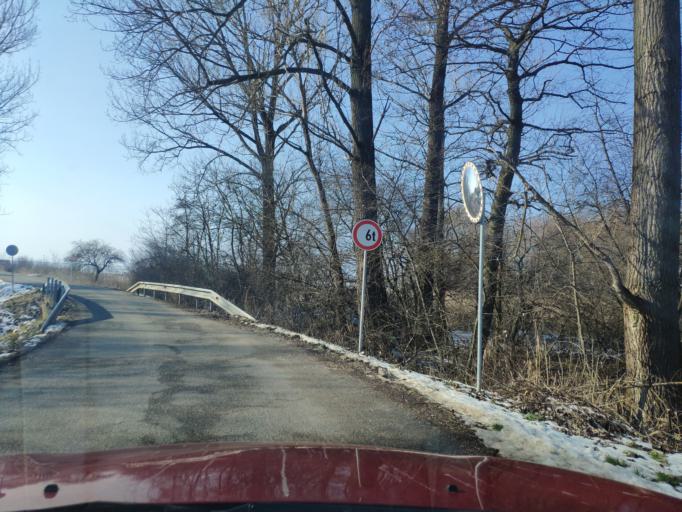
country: HU
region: Borsod-Abauj-Zemplen
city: Gonc
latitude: 48.5846
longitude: 21.2710
